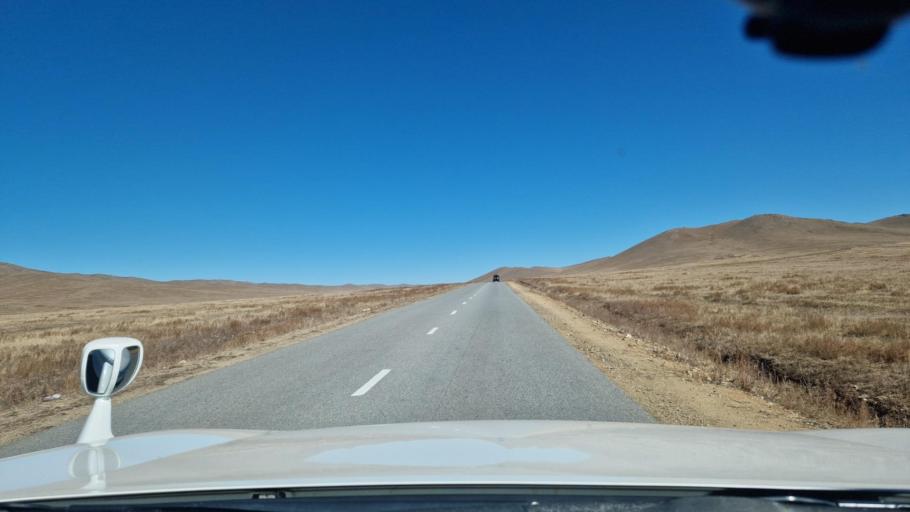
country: MN
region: Central Aimak
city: Bayandelger
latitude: 47.7071
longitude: 108.5651
